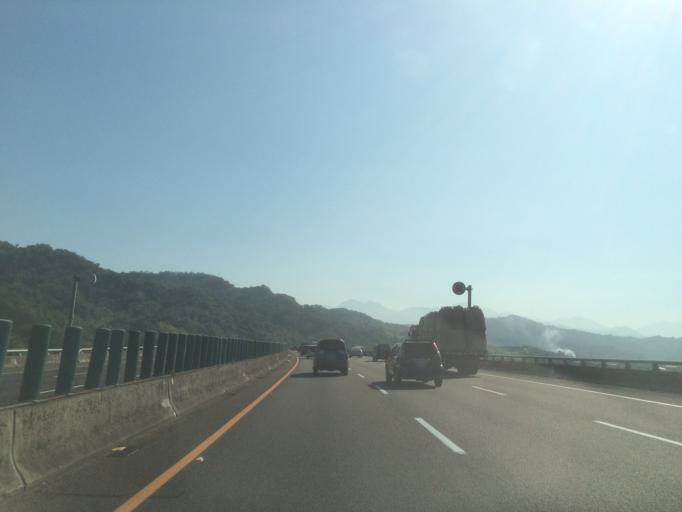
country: TW
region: Taiwan
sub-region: Nantou
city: Nantou
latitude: 23.9124
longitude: 120.6955
